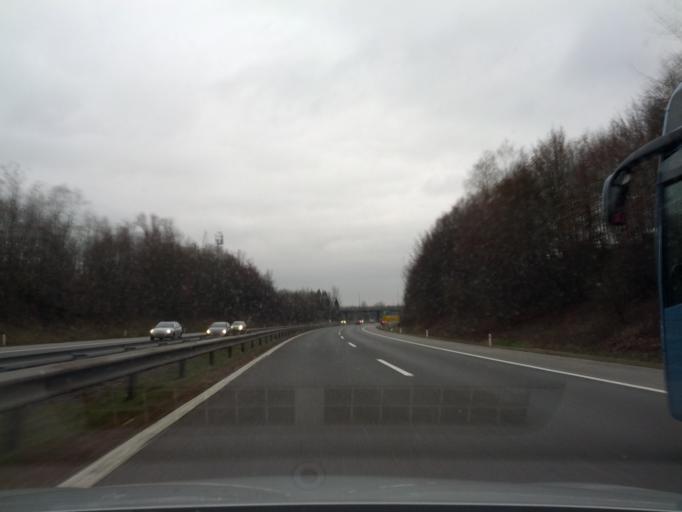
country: SI
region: Medvode
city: Zgornje Pirnice
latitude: 46.1273
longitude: 14.4825
